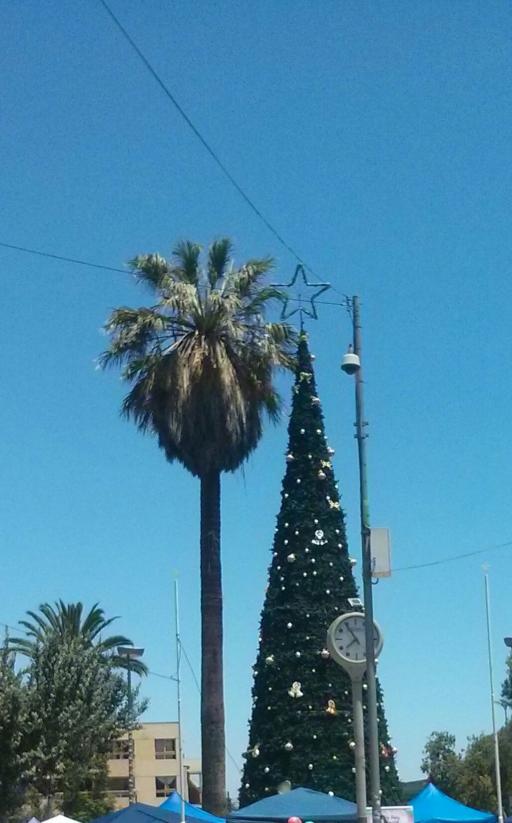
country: CL
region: Atacama
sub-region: Provincia de Copiapo
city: Copiapo
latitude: -26.9959
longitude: -70.7867
